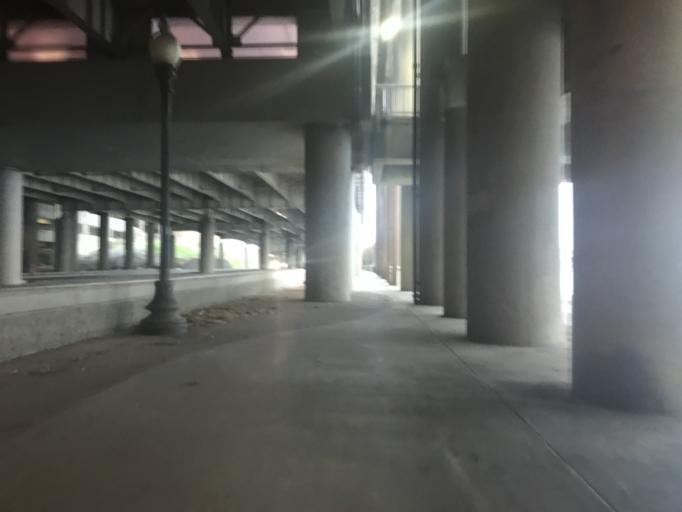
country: US
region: Kentucky
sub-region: Jefferson County
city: Louisville
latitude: 38.2591
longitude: -85.7571
